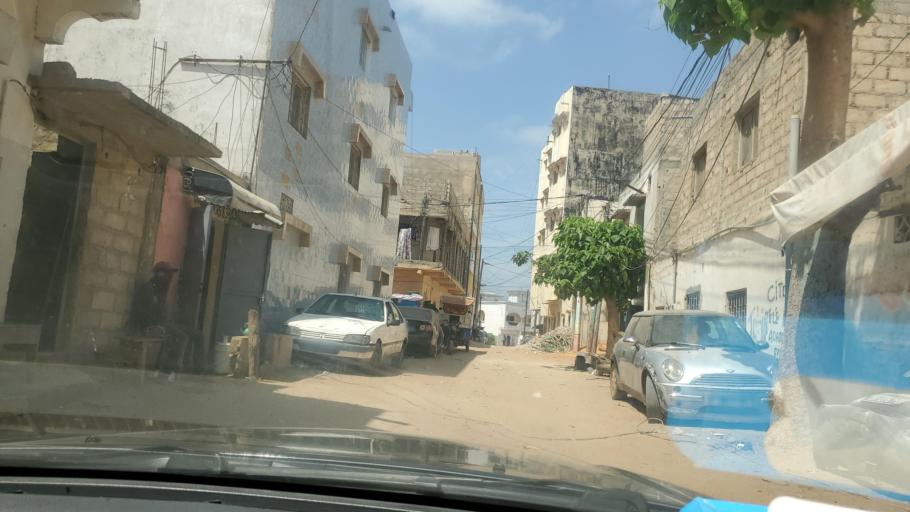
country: SN
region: Dakar
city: Grand Dakar
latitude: 14.7302
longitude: -17.4557
